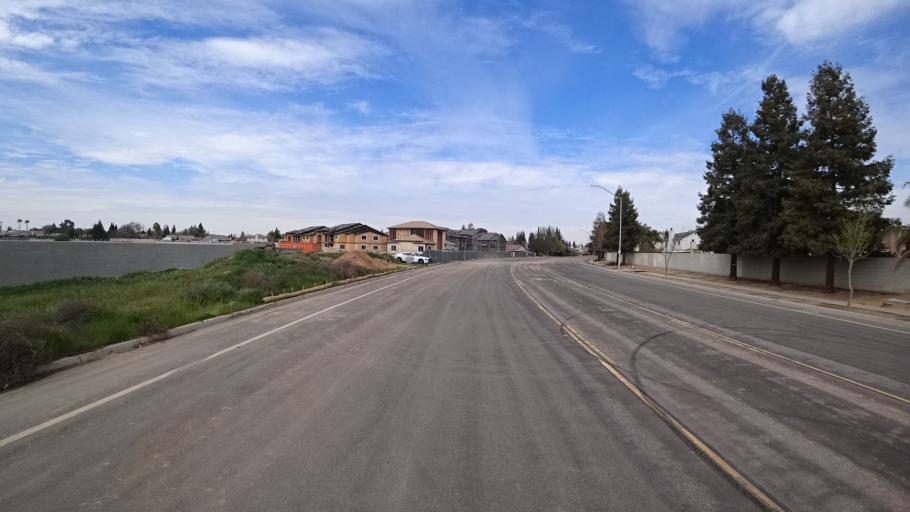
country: US
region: California
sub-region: Fresno County
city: West Park
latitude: 36.8173
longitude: -119.8822
